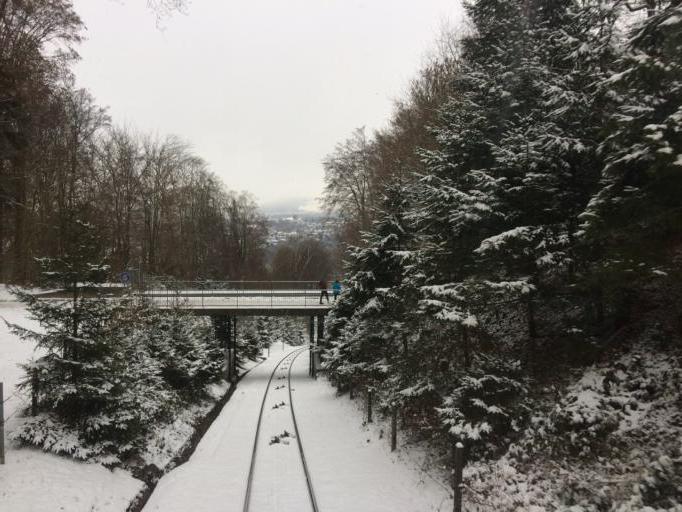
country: CH
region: Bern
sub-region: Bern-Mittelland District
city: Bern
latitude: 46.9246
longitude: 7.4433
